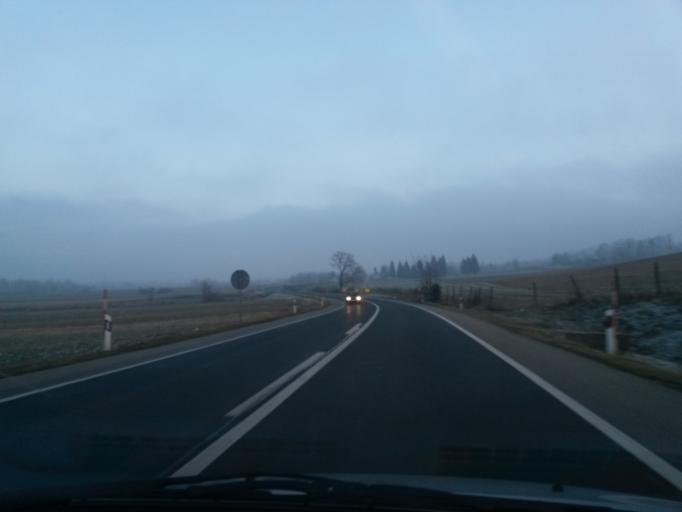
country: HR
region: Varazdinska
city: Ludbreg
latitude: 46.2153
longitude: 16.6888
